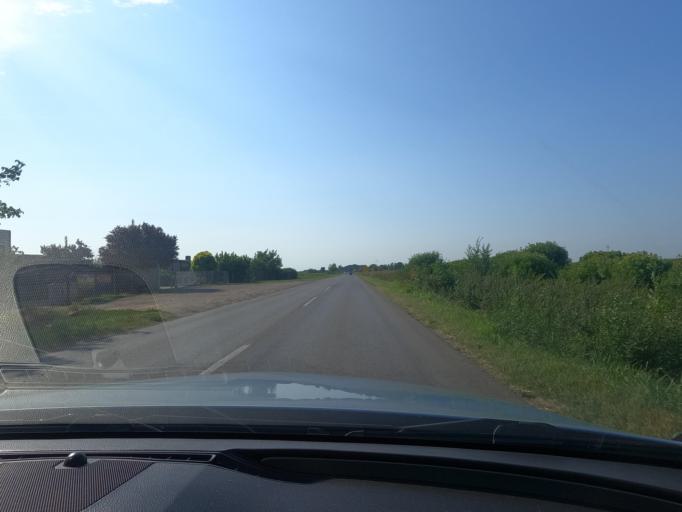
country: RS
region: Autonomna Pokrajina Vojvodina
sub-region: Juznobacki Okrug
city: Kovilj
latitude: 45.2870
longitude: 19.9681
